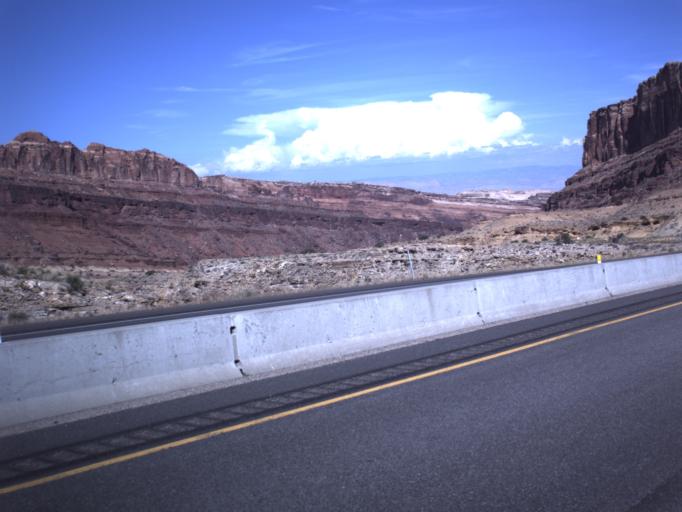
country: US
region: Utah
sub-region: Carbon County
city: East Carbon City
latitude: 38.9375
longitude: -110.4690
